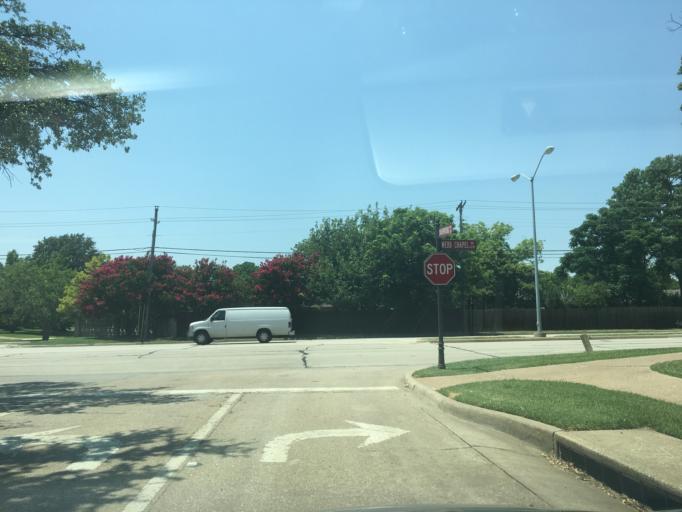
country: US
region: Texas
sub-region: Dallas County
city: Carrollton
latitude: 32.9482
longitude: -96.8705
